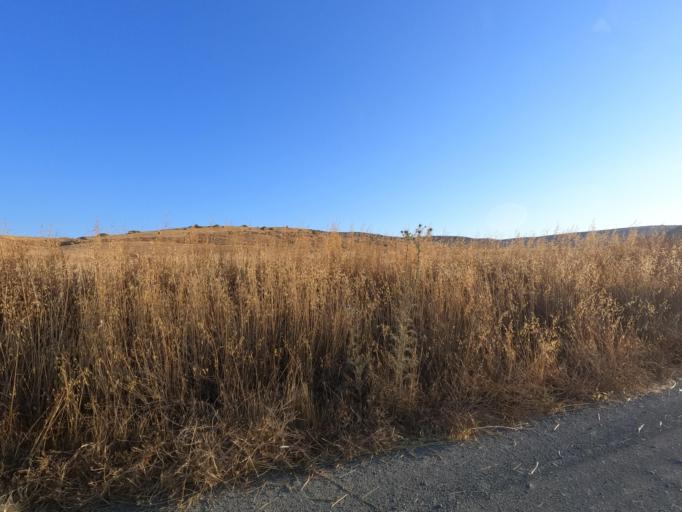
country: CY
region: Larnaka
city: Troulloi
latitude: 35.0317
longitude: 33.6454
